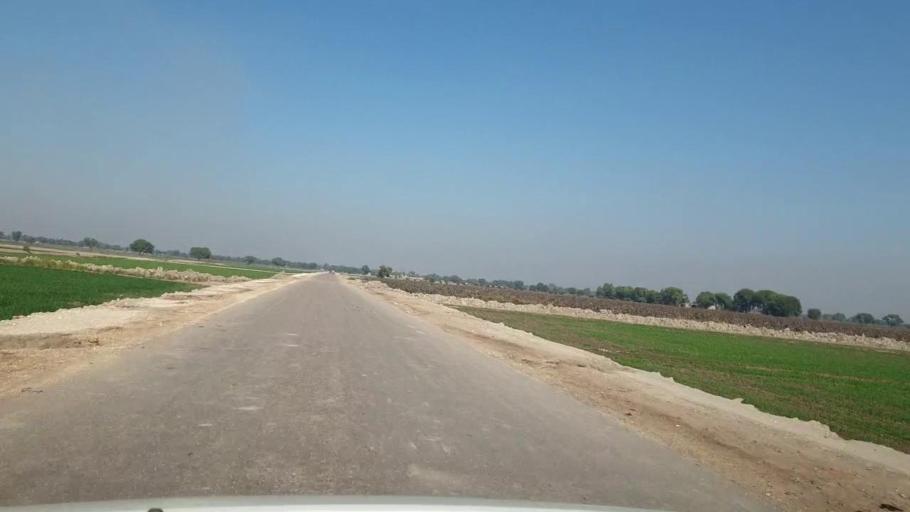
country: PK
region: Sindh
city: Bhan
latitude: 26.6554
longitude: 67.7062
